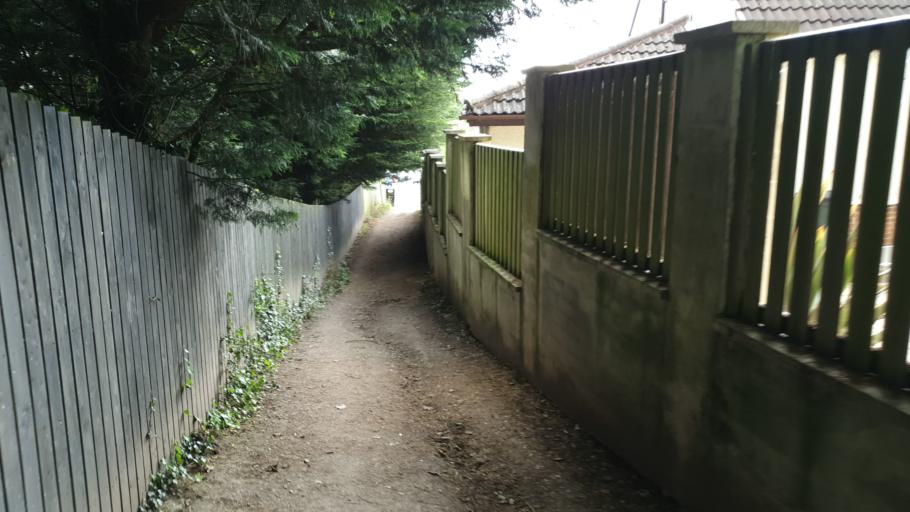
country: GB
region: England
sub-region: City and Borough of Leeds
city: Guiseley
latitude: 53.8821
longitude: -1.7157
